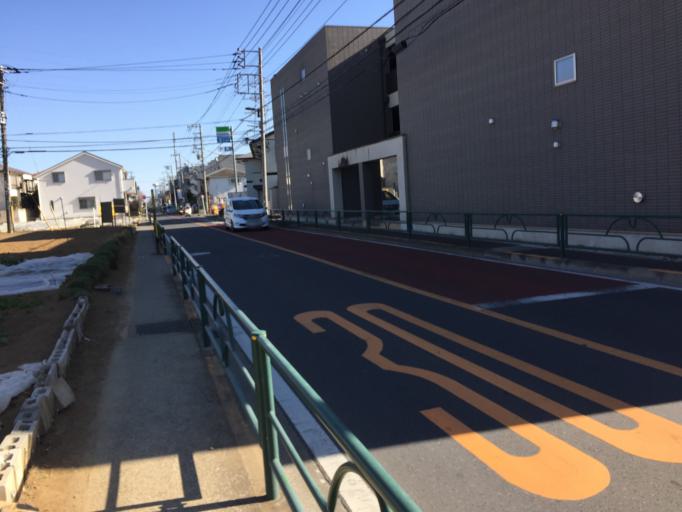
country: JP
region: Tokyo
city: Chofugaoka
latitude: 35.6271
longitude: 139.5858
